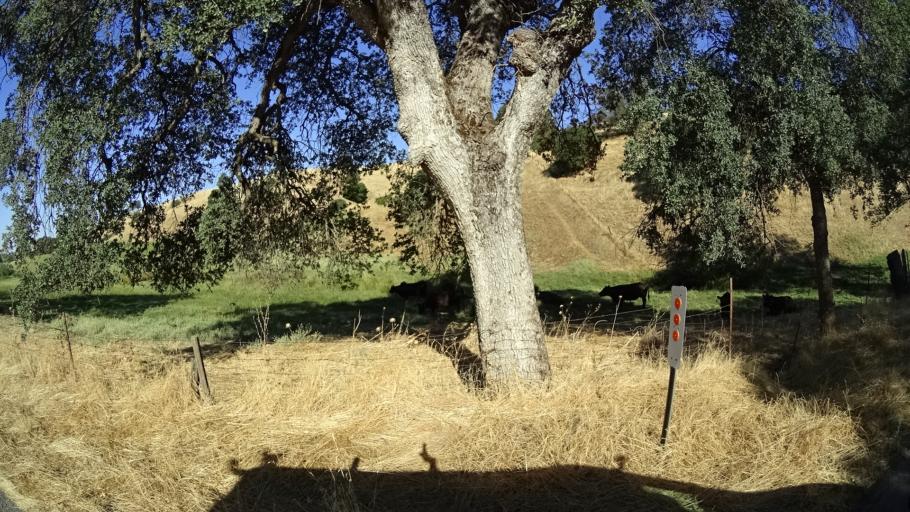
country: US
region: California
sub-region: Calaveras County
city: Angels Camp
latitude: 38.0518
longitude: -120.5074
